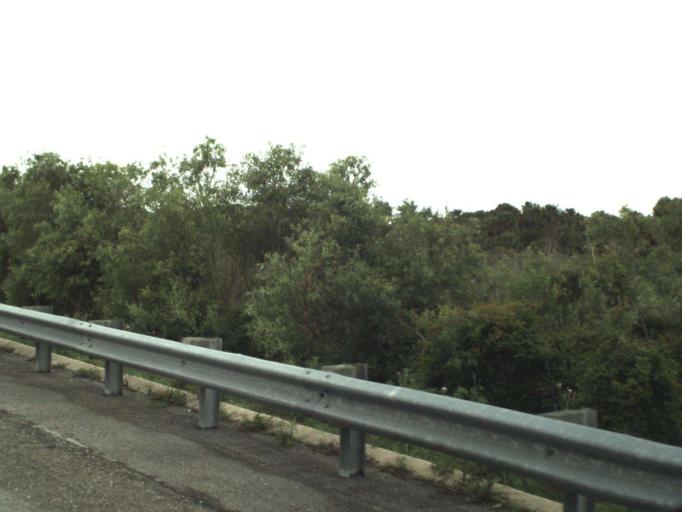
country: US
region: Florida
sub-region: Brevard County
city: Mims
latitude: 28.6657
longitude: -80.9082
